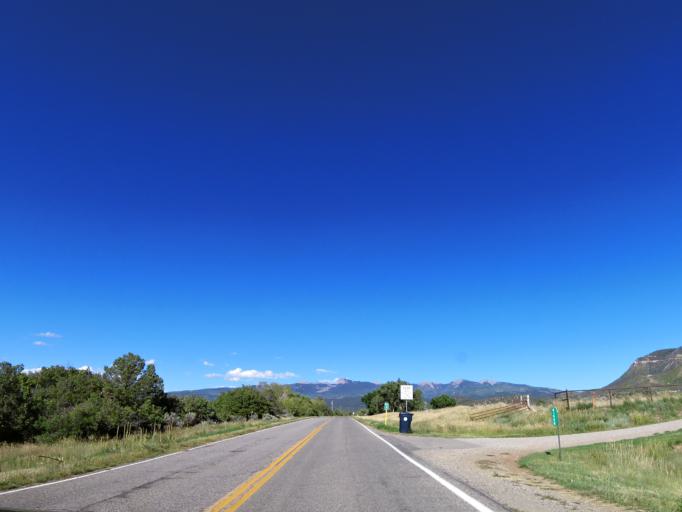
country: US
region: Colorado
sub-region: Montezuma County
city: Mancos
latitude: 37.3450
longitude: -108.2804
